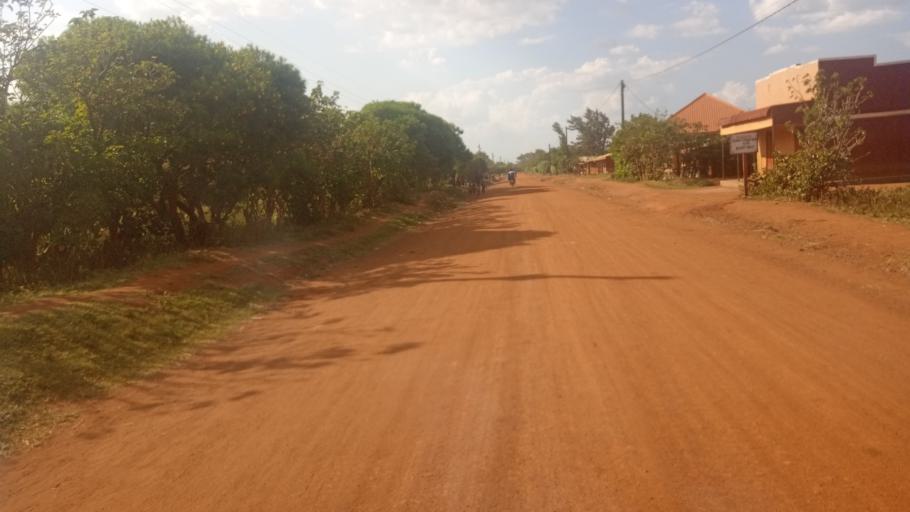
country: UG
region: Eastern Region
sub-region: Kween District
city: Binyin
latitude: 1.5056
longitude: 34.5002
